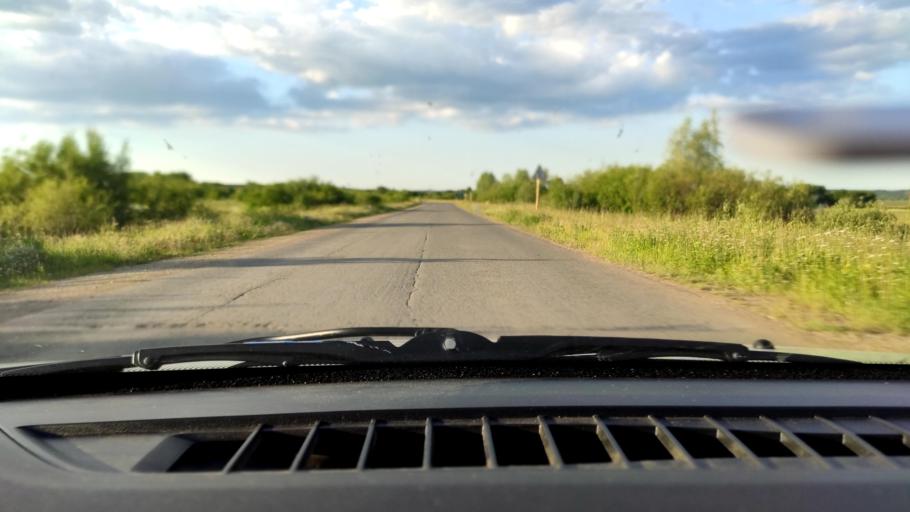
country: RU
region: Perm
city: Uinskoye
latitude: 57.0837
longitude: 56.5560
